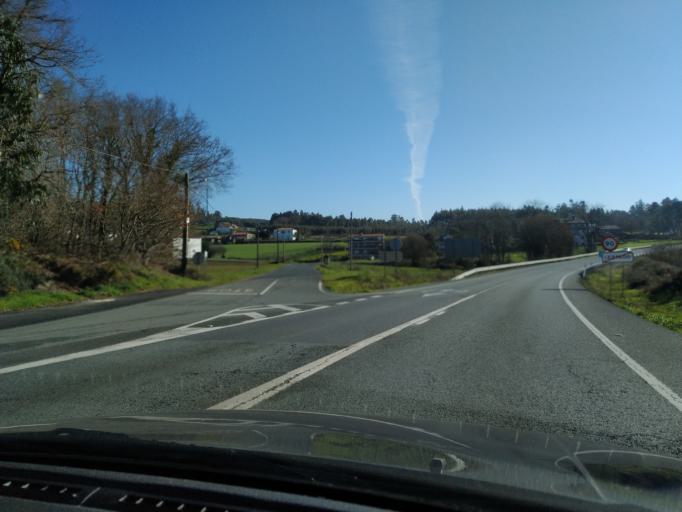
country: ES
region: Galicia
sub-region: Provincia da Coruna
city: Vedra
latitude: 42.7955
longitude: -8.4654
